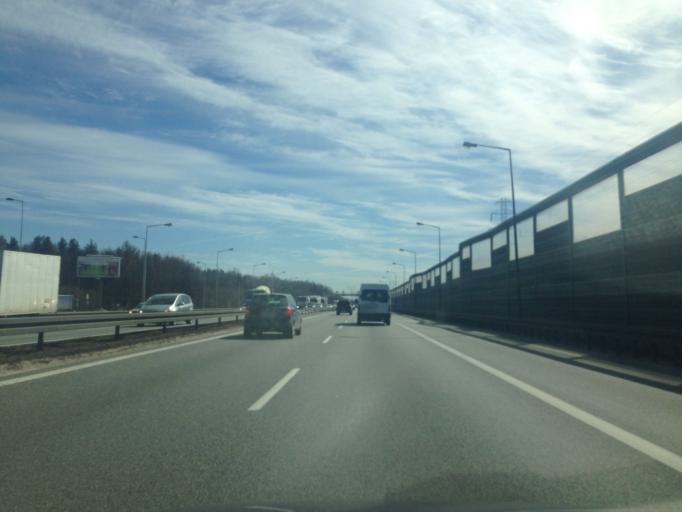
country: PL
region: Pomeranian Voivodeship
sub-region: Gdynia
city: Wielki Kack
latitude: 54.4257
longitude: 18.4877
